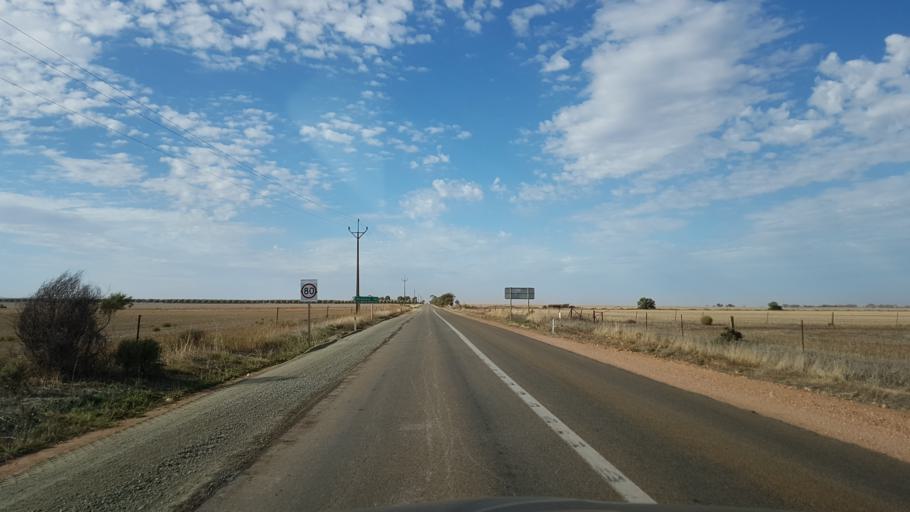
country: AU
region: South Australia
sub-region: Clare and Gilbert Valleys
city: Clare
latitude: -33.8512
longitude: 138.4759
